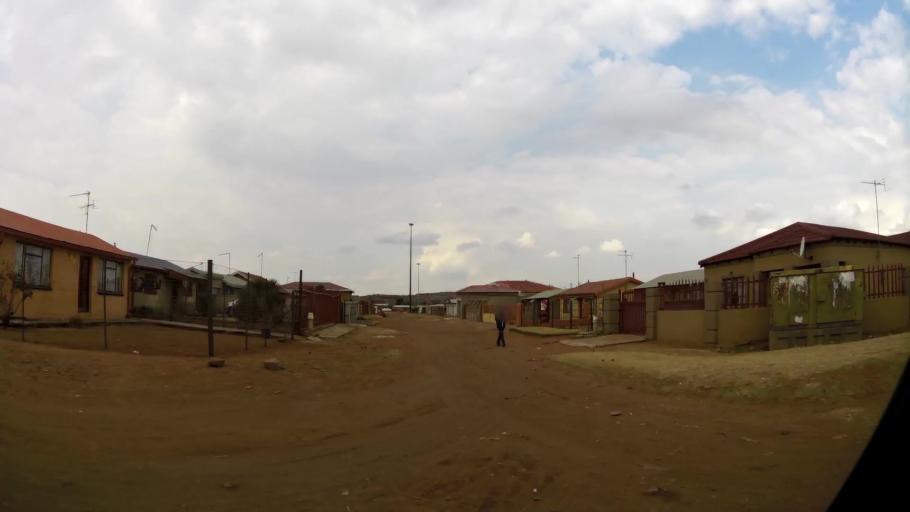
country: ZA
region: Gauteng
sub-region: Sedibeng District Municipality
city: Vanderbijlpark
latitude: -26.6646
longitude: 27.8532
